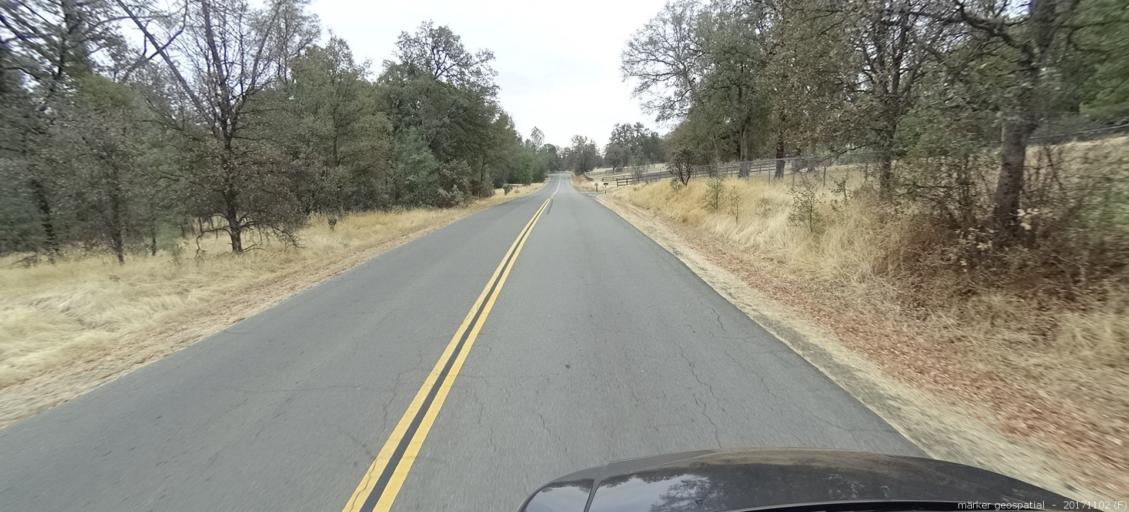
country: US
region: California
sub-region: Shasta County
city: Shasta Lake
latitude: 40.6556
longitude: -122.3181
